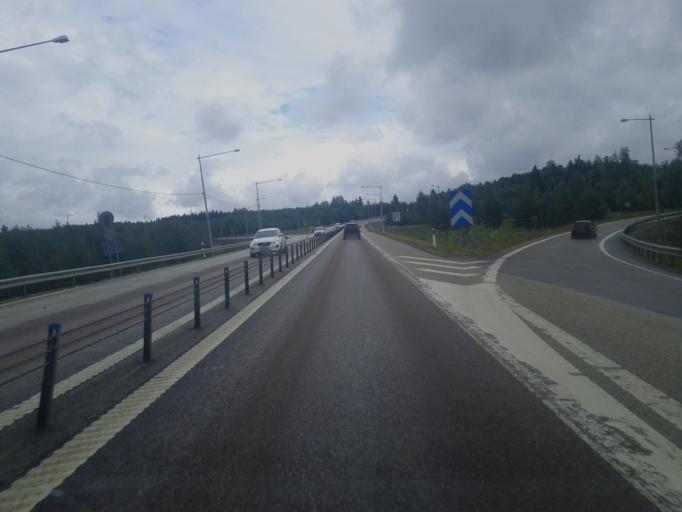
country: SE
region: Vaesternorrland
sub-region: Timra Kommun
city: Soraker
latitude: 62.5239
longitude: 17.4734
